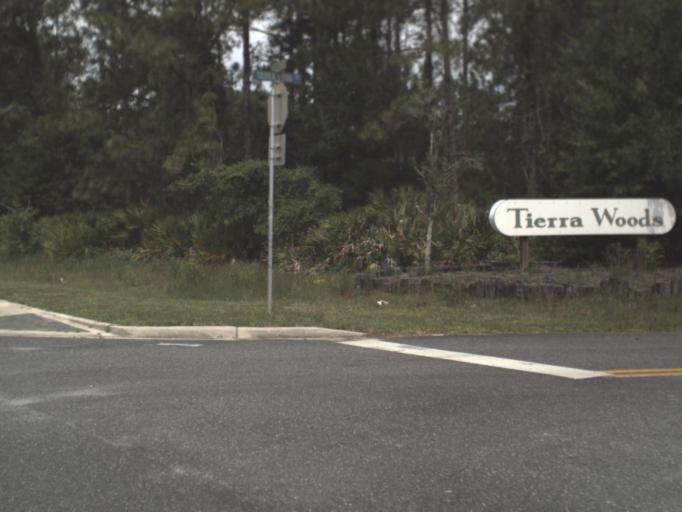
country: US
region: Florida
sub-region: Putnam County
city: Palatka
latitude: 29.6370
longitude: -81.7022
